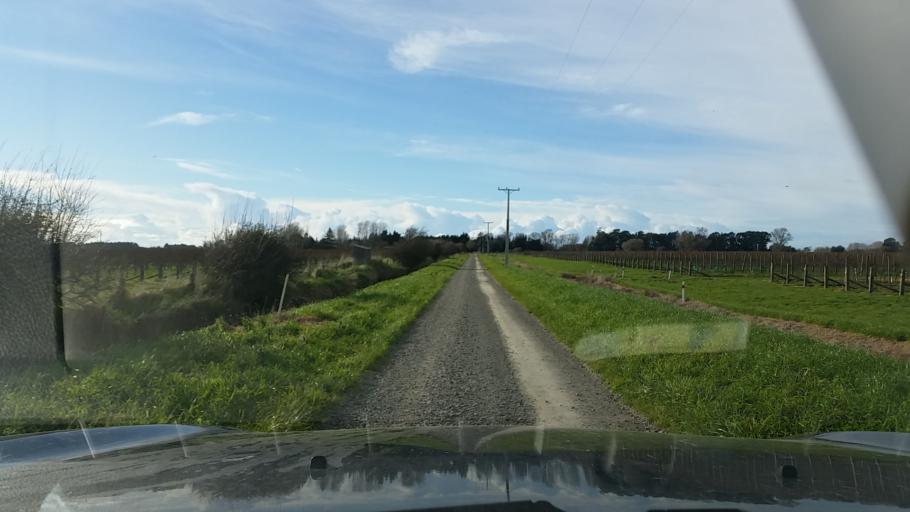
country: NZ
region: Marlborough
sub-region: Marlborough District
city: Blenheim
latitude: -41.4307
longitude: 173.9862
